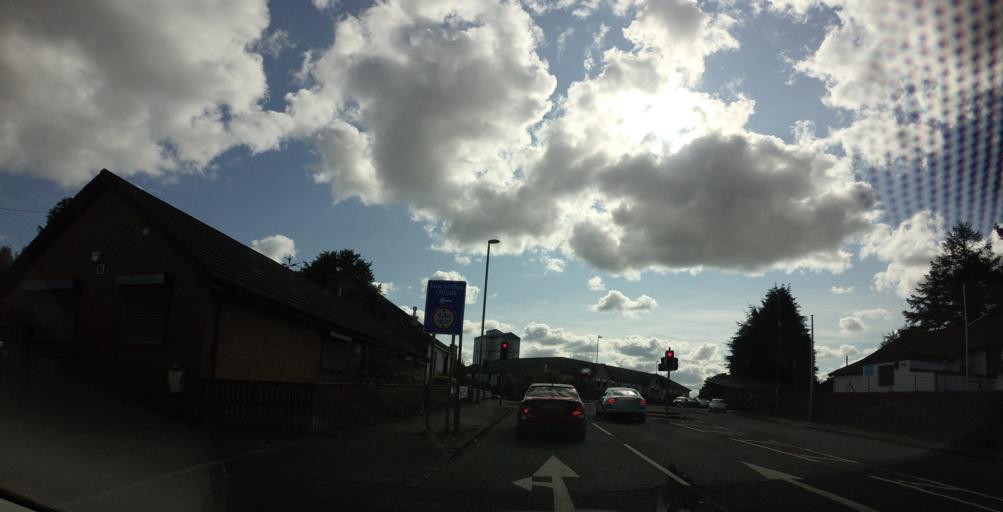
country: GB
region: Scotland
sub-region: North Lanarkshire
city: Coatbridge
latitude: 55.8558
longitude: -4.0472
